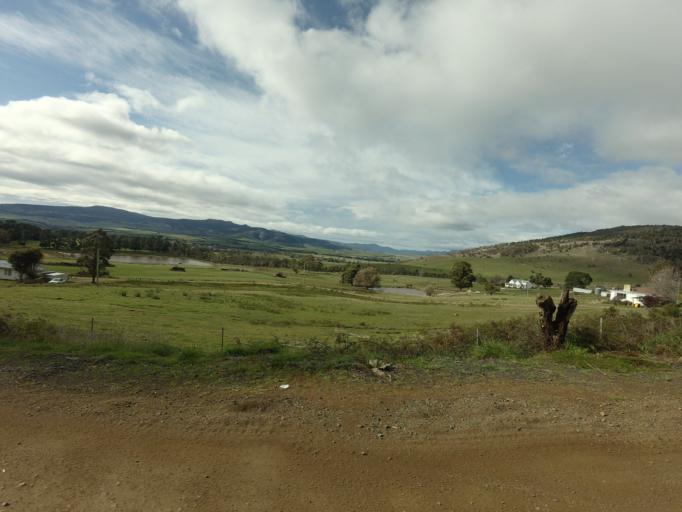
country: AU
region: Tasmania
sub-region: Derwent Valley
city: New Norfolk
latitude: -42.7207
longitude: 146.8736
